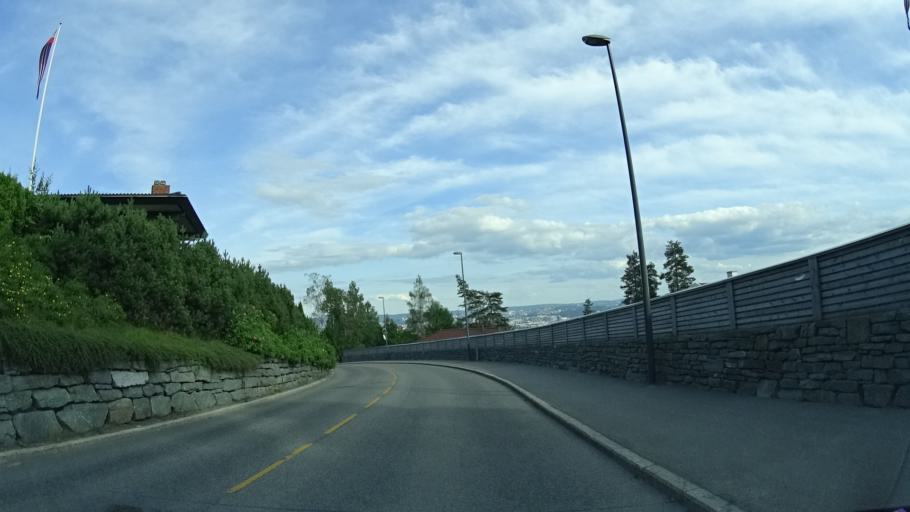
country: NO
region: Oslo
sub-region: Oslo
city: Sjolyststranda
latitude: 59.9585
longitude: 10.6710
